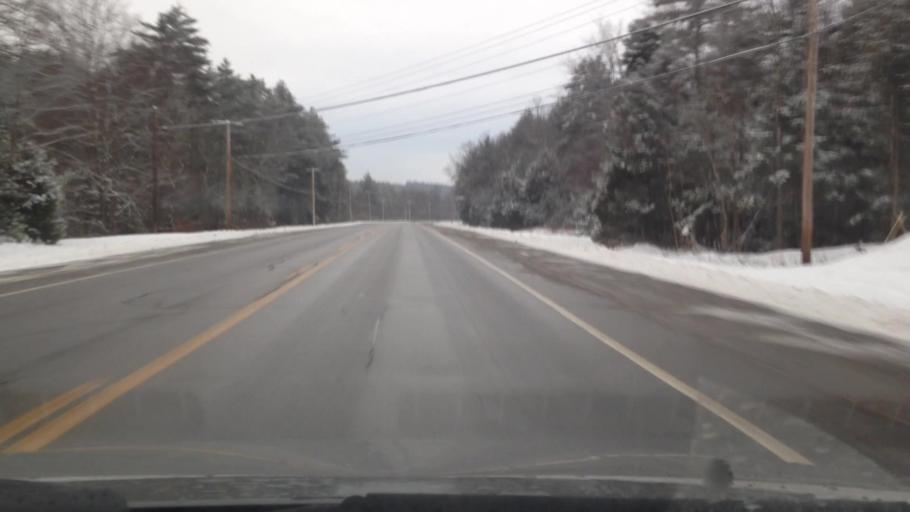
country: US
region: New Hampshire
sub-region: Cheshire County
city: Keene
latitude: 42.9840
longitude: -72.2574
